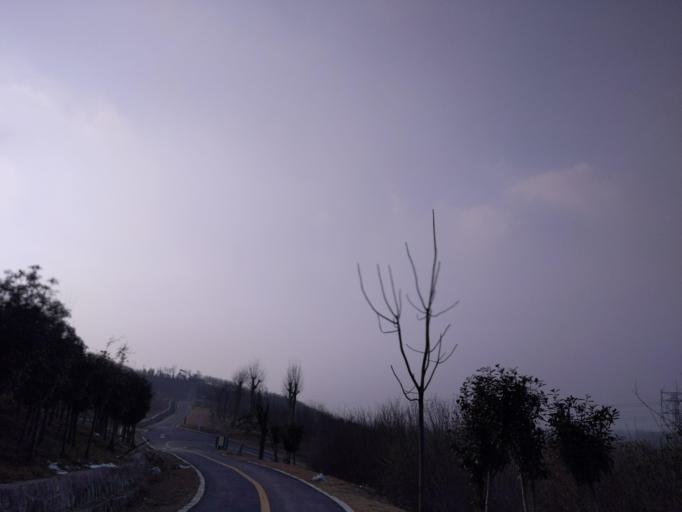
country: CN
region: Henan Sheng
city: Puyang
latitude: 35.8202
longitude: 115.0194
